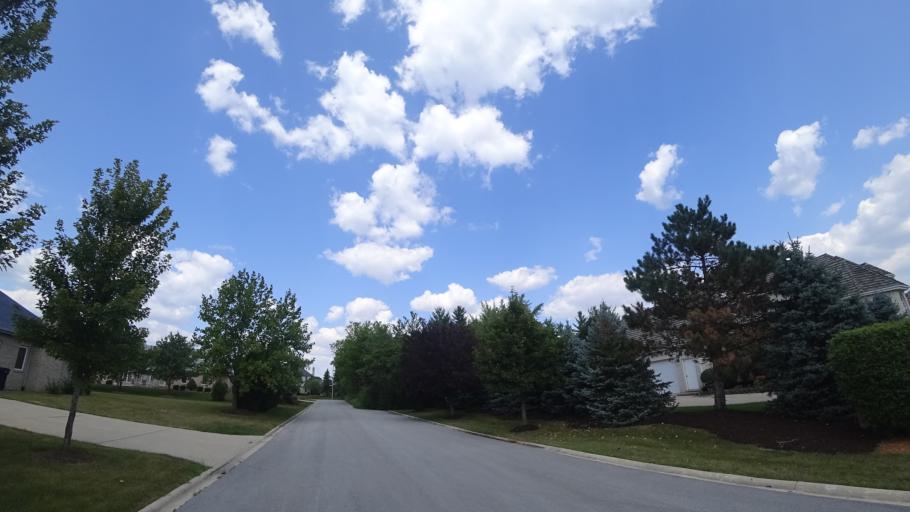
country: US
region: Illinois
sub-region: Cook County
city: Orland Park
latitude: 41.6280
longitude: -87.8172
